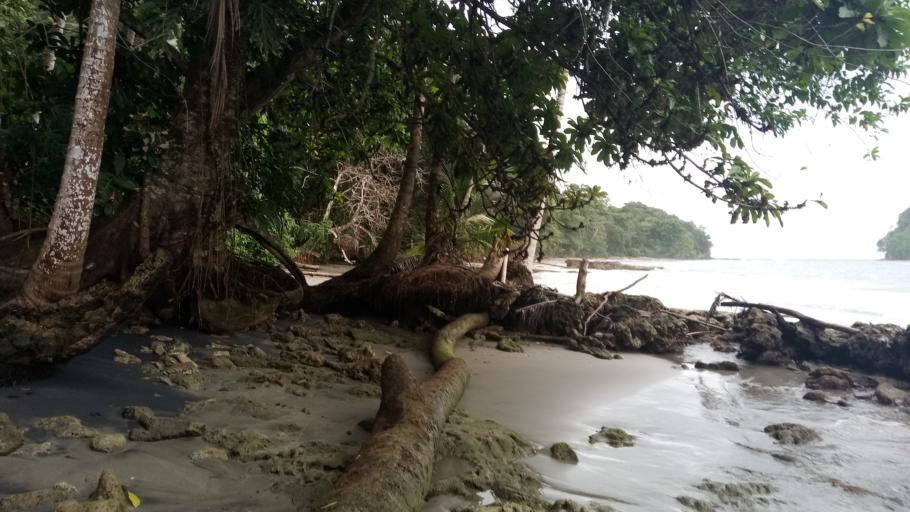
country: CR
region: Limon
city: Sixaola
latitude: 9.6260
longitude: -82.6199
